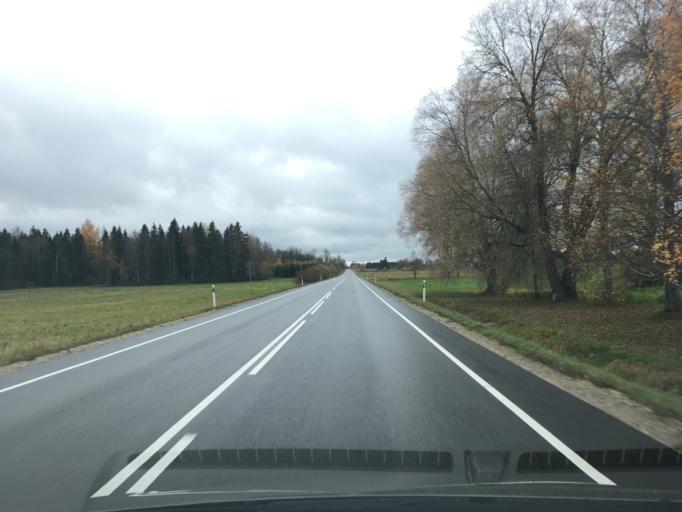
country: EE
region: Jogevamaa
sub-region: Tabivere vald
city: Tabivere
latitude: 58.4552
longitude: 26.5296
